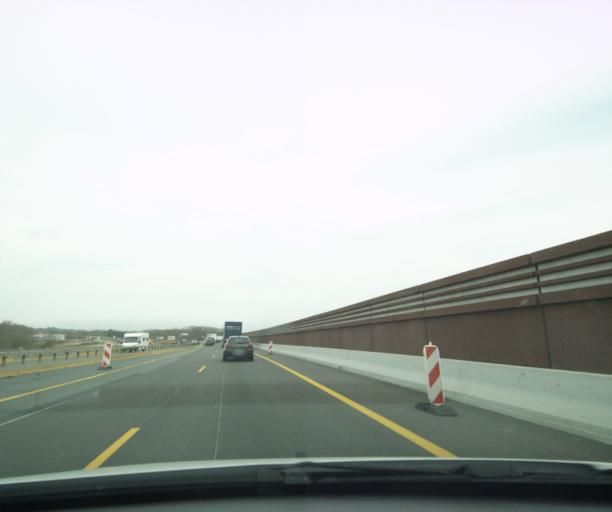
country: FR
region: Aquitaine
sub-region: Departement des Pyrenees-Atlantiques
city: Bidart
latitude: 43.4318
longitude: -1.5783
